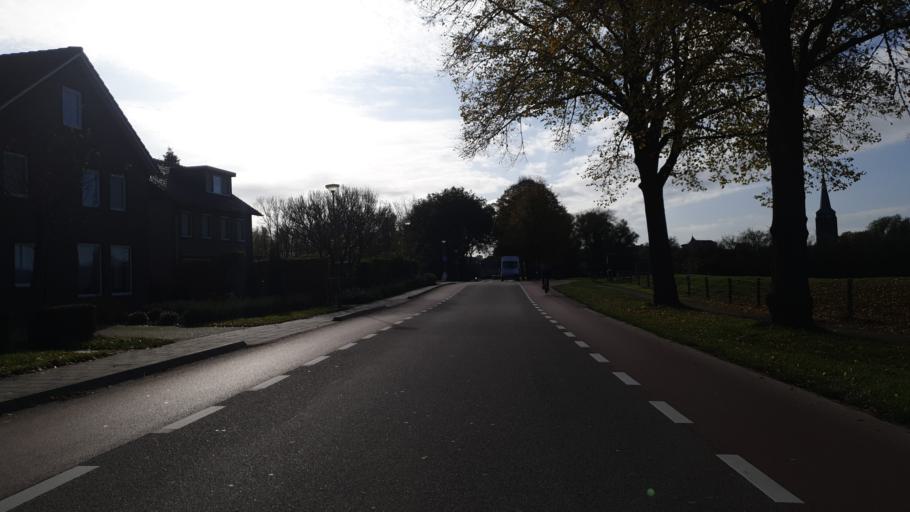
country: NL
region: Limburg
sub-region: Gemeente Gennep
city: Gennep
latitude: 51.7049
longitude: 5.9724
